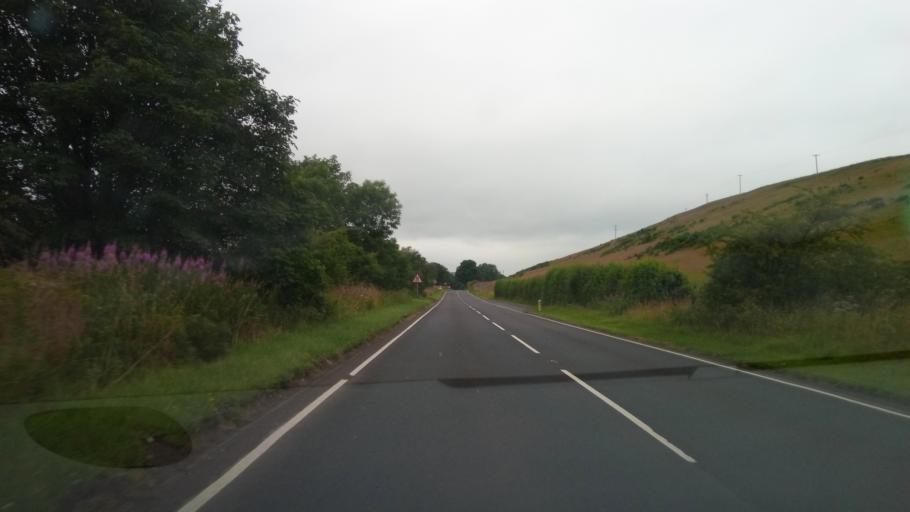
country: GB
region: Scotland
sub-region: The Scottish Borders
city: Hawick
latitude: 55.3814
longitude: -2.8703
